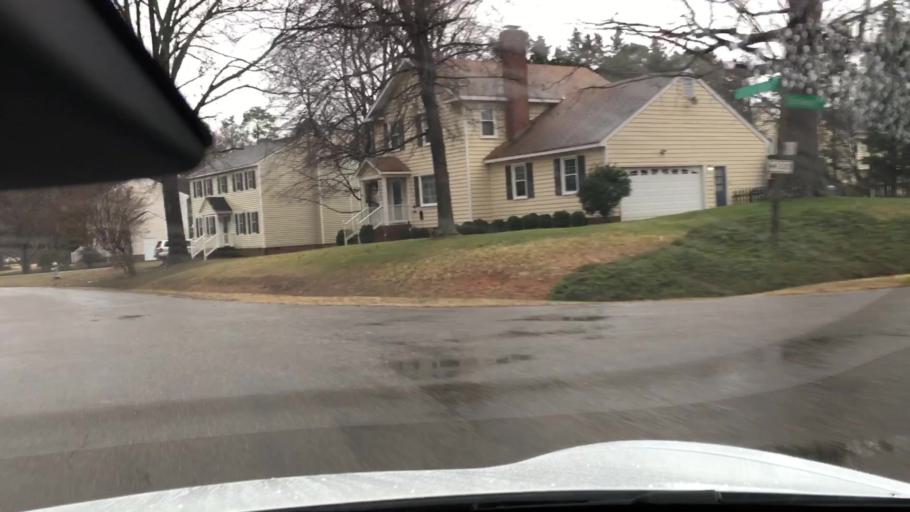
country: US
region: Virginia
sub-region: Chesterfield County
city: Bon Air
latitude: 37.5314
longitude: -77.5960
